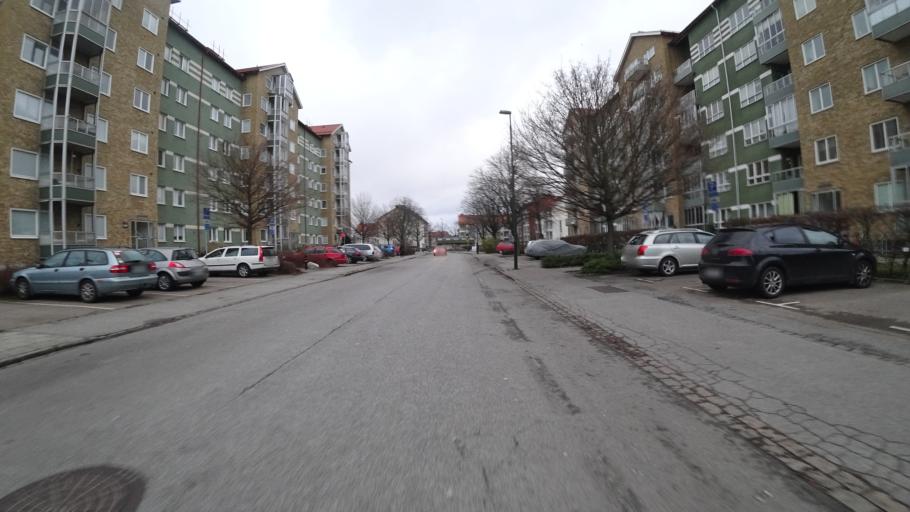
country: SE
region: Skane
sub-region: Burlovs Kommun
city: Arloev
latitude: 55.5951
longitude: 13.0454
